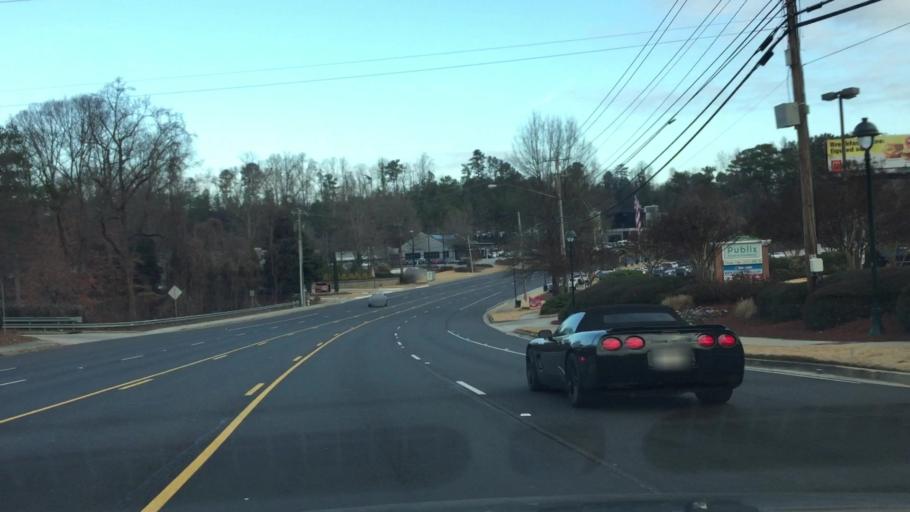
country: US
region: Georgia
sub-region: DeKalb County
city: Dunwoody
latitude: 33.9606
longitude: -84.3656
